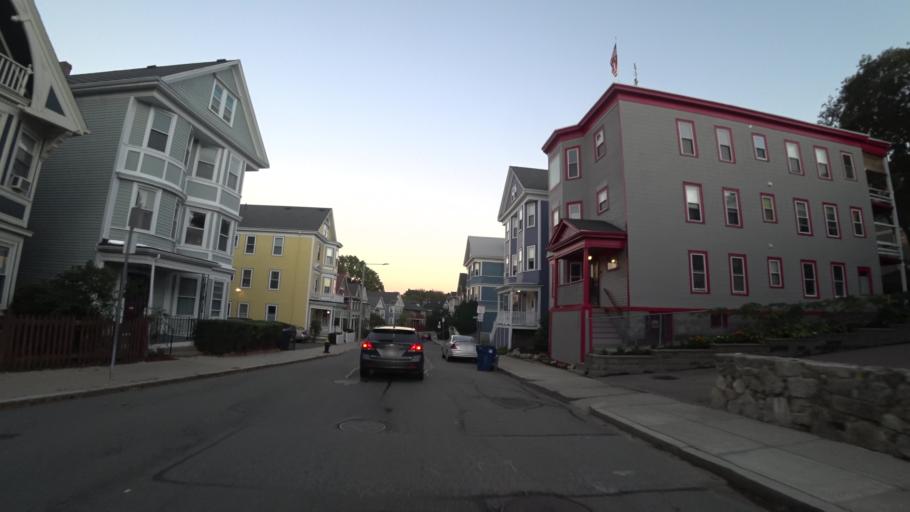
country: US
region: Massachusetts
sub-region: Norfolk County
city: Brookline
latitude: 42.3297
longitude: -71.1025
